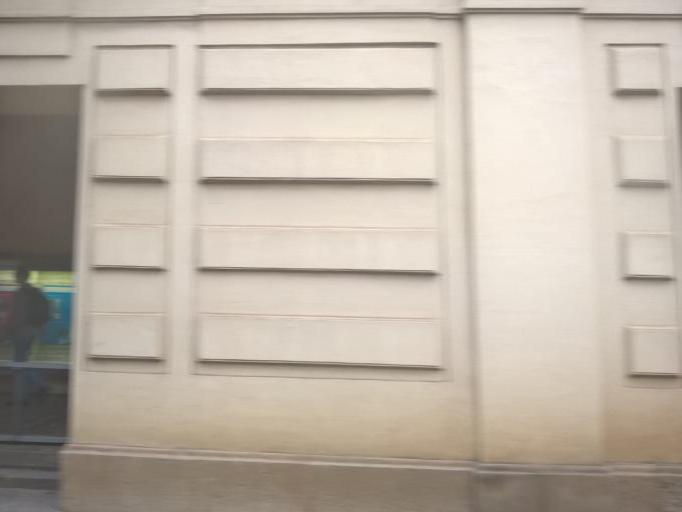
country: CZ
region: Praha
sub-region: Praha 1
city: Mala Strana
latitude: 50.0844
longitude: 14.4044
